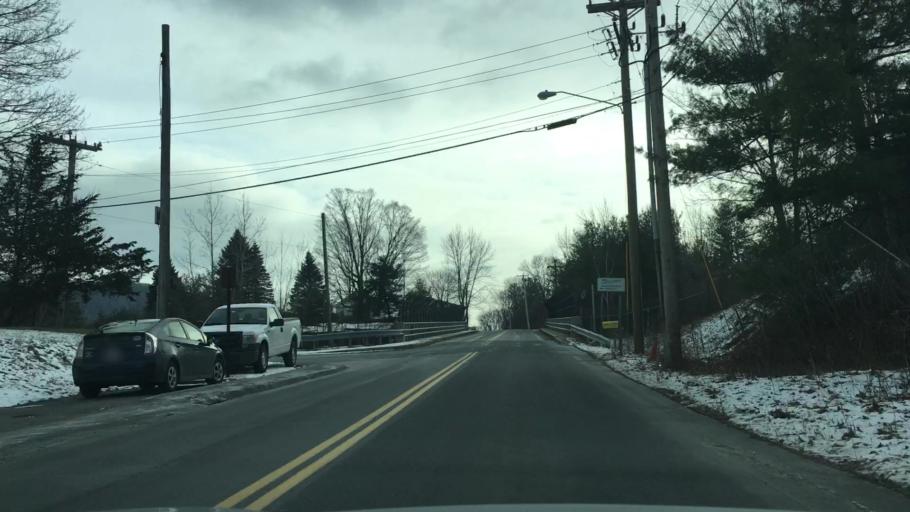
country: US
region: Massachusetts
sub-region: Berkshire County
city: Lee
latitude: 42.2977
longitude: -73.2489
